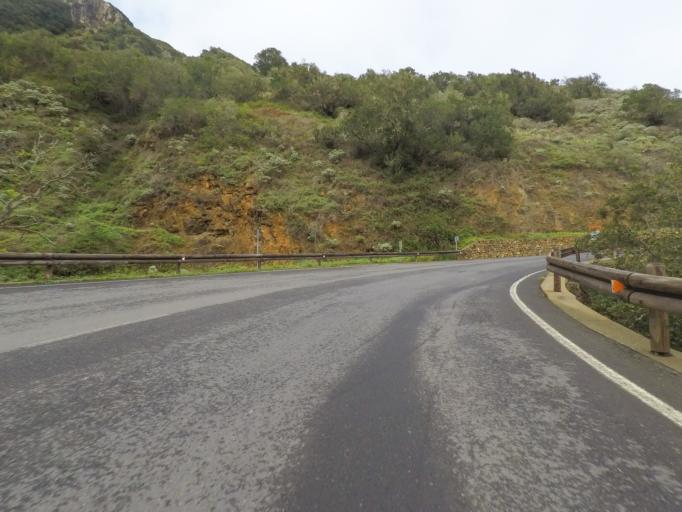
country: ES
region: Canary Islands
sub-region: Provincia de Santa Cruz de Tenerife
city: Vallehermosa
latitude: 28.1572
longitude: -17.2884
